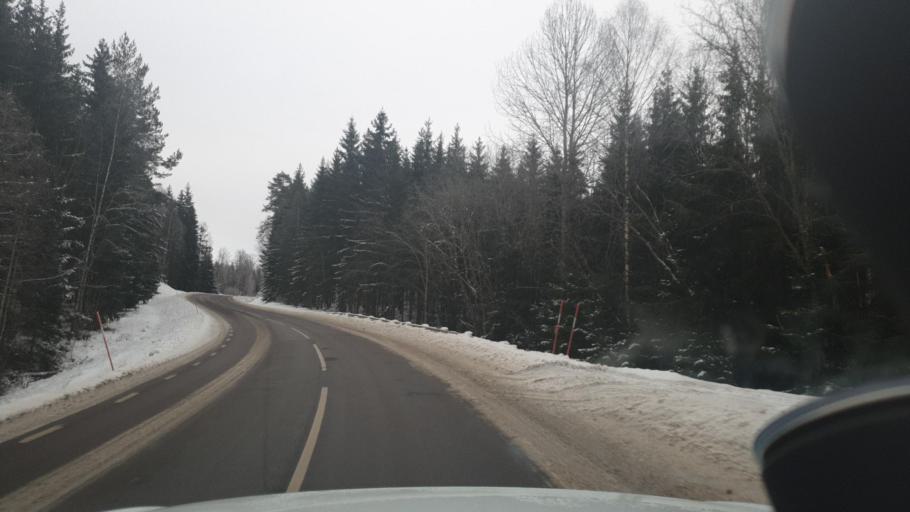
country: SE
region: Vaermland
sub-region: Eda Kommun
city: Amotfors
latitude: 59.7825
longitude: 12.2608
